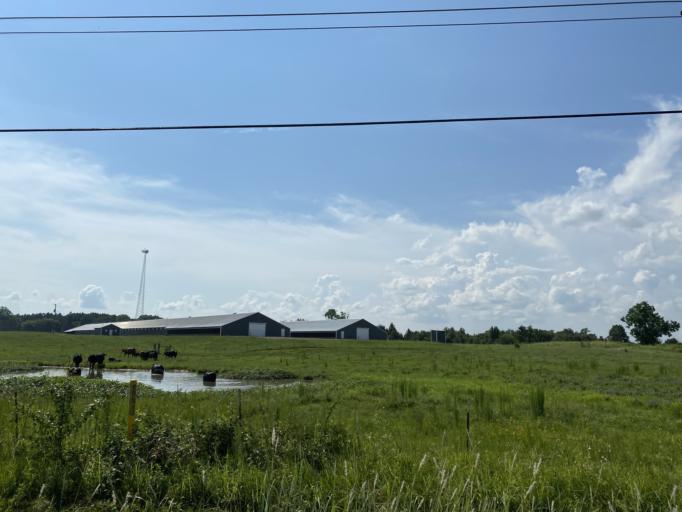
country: US
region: Alabama
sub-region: Lawrence County
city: Town Creek
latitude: 34.6310
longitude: -87.4088
